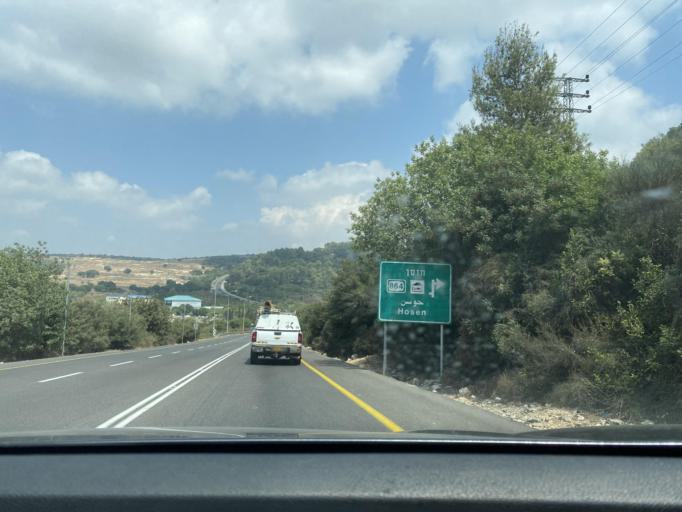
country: IL
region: Northern District
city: Kefar Weradim
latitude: 33.0027
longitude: 35.2898
